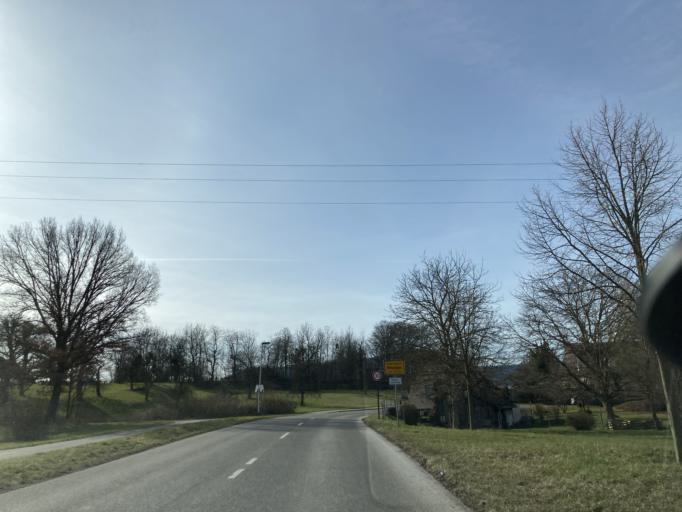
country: DE
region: Baden-Wuerttemberg
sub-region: Tuebingen Region
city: Nehren
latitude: 48.4163
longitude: 9.0666
